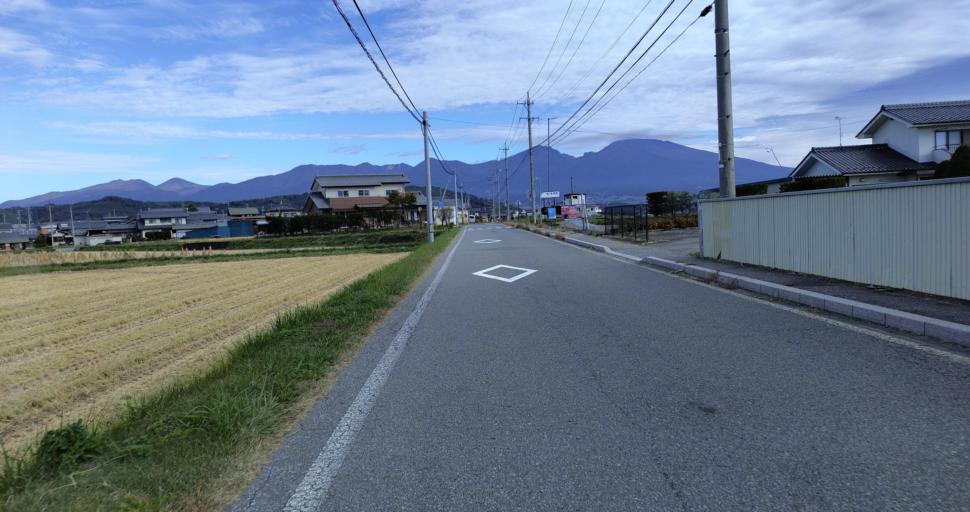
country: JP
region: Nagano
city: Komoro
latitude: 36.2698
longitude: 138.4053
